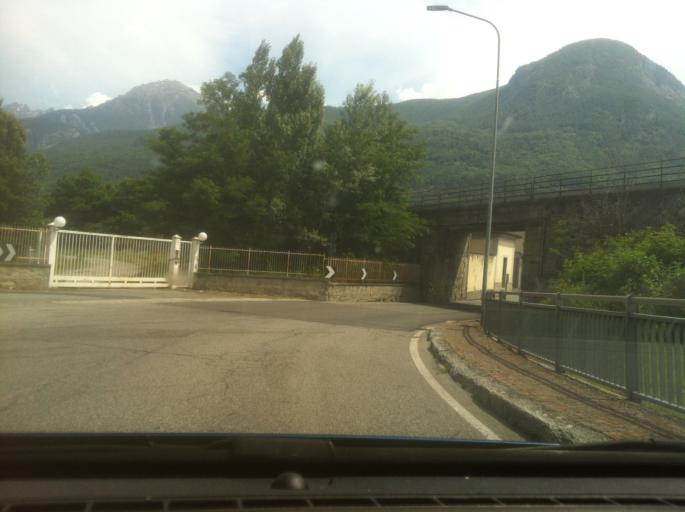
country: IT
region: Aosta Valley
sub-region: Valle d'Aosta
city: Saint Marcel
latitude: 45.7393
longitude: 7.4406
